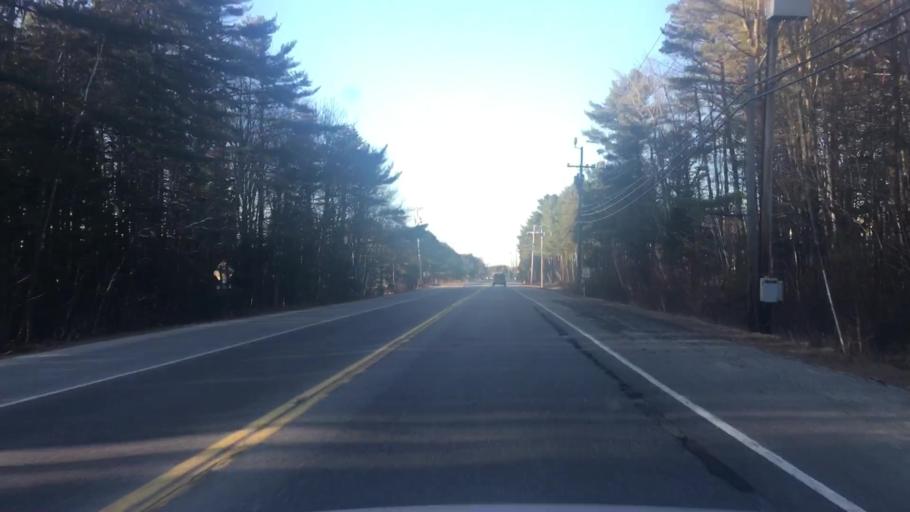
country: US
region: Maine
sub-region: Cumberland County
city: Brunswick
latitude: 43.8990
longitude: -69.9093
